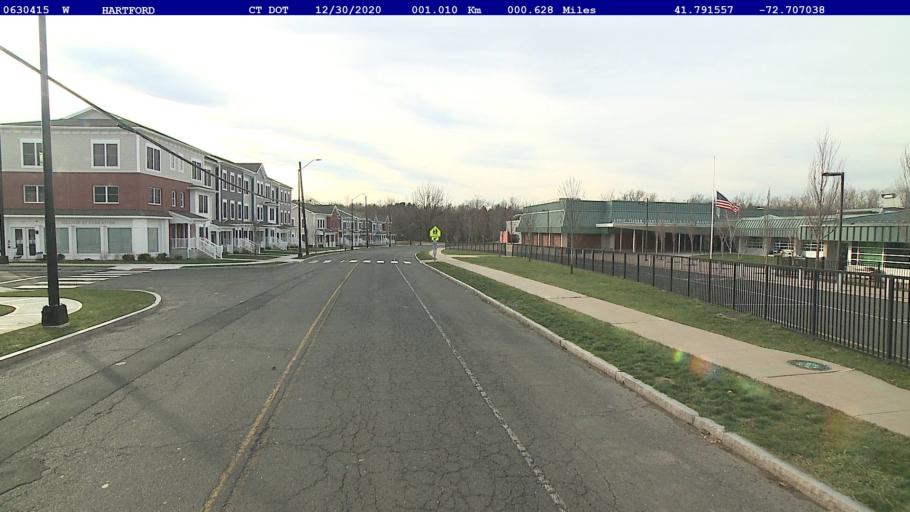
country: US
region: Connecticut
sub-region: Hartford County
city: Blue Hills
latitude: 41.7916
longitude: -72.7070
